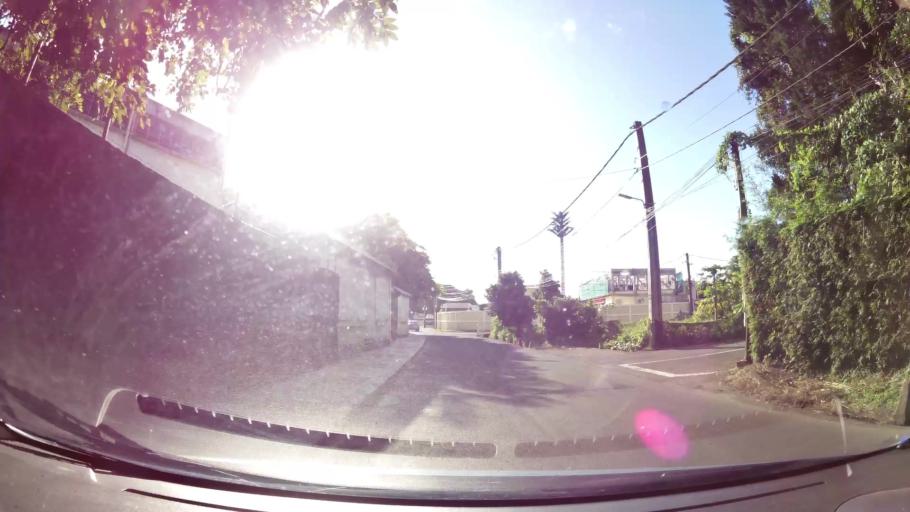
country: MU
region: Plaines Wilhems
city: Vacoas
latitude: -20.3092
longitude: 57.4952
